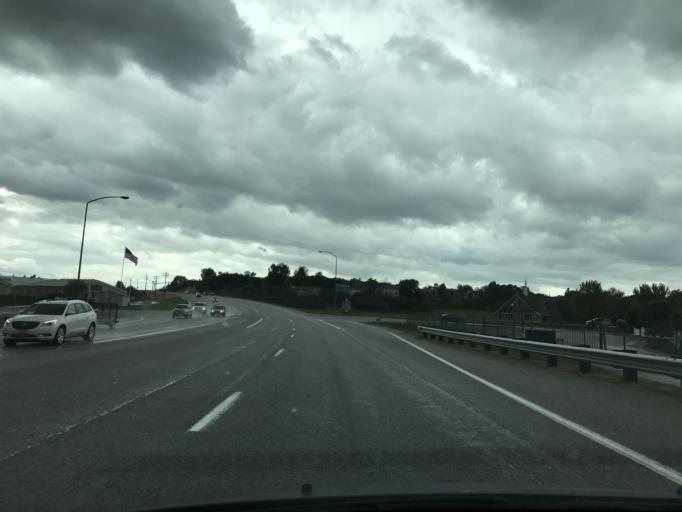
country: US
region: Utah
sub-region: Davis County
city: South Weber
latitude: 41.1081
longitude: -111.9144
